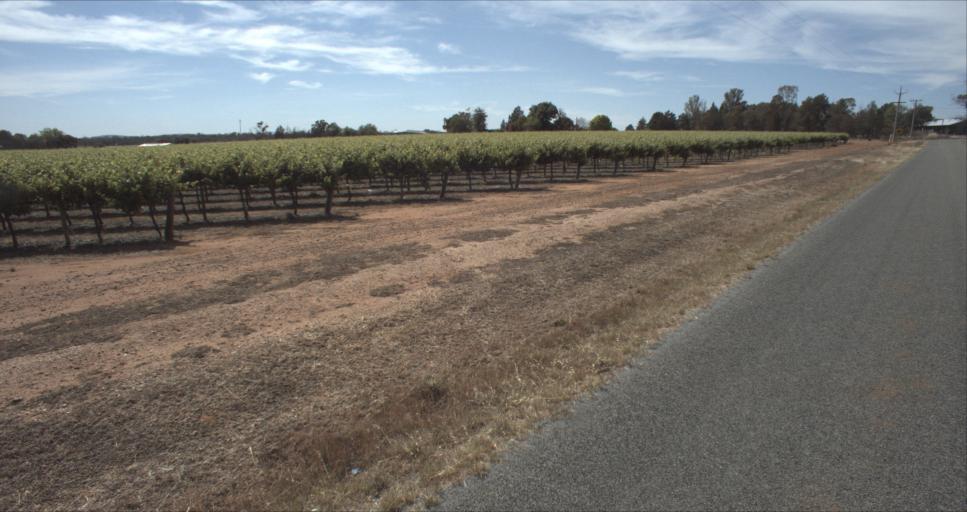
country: AU
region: New South Wales
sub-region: Leeton
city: Leeton
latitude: -34.5695
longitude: 146.4451
